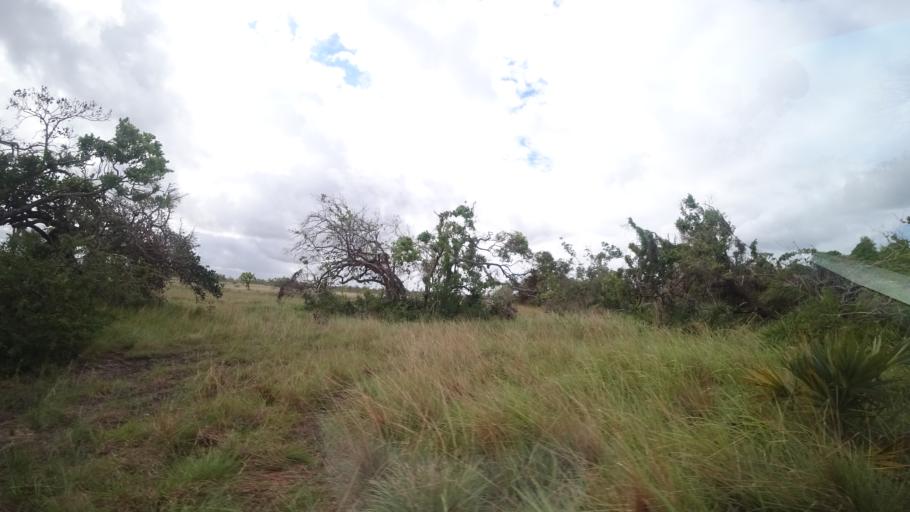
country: MZ
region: Sofala
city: Beira
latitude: -19.6122
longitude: 35.2190
